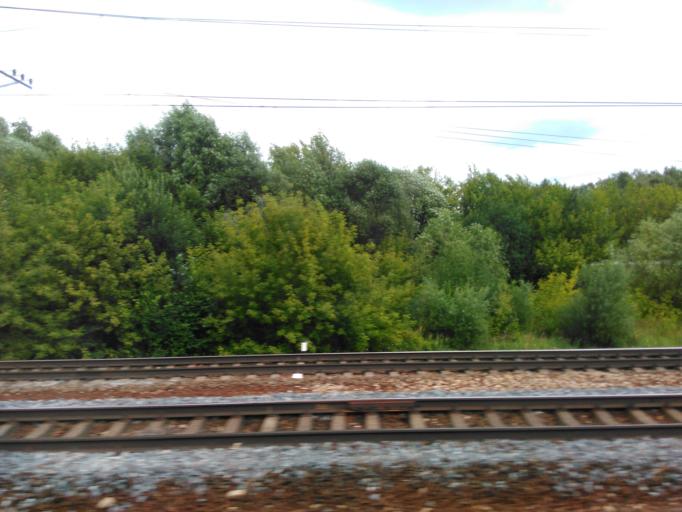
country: RU
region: Moscow
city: Rostokino
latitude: 55.8372
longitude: 37.6711
